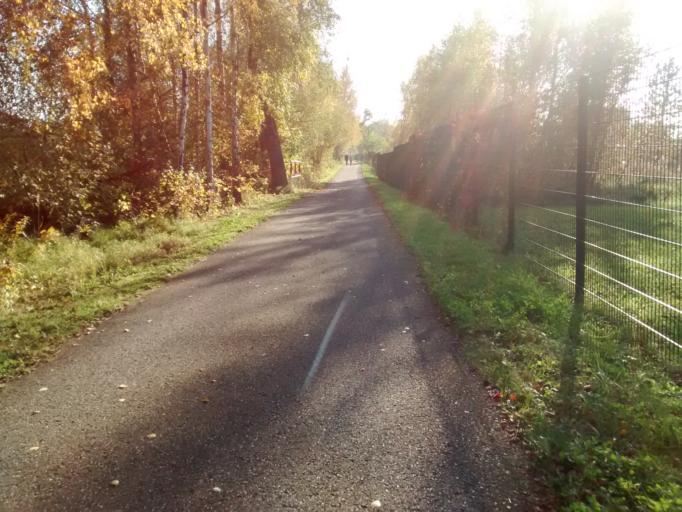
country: DE
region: Brandenburg
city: Hennigsdorf
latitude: 52.6273
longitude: 13.2161
